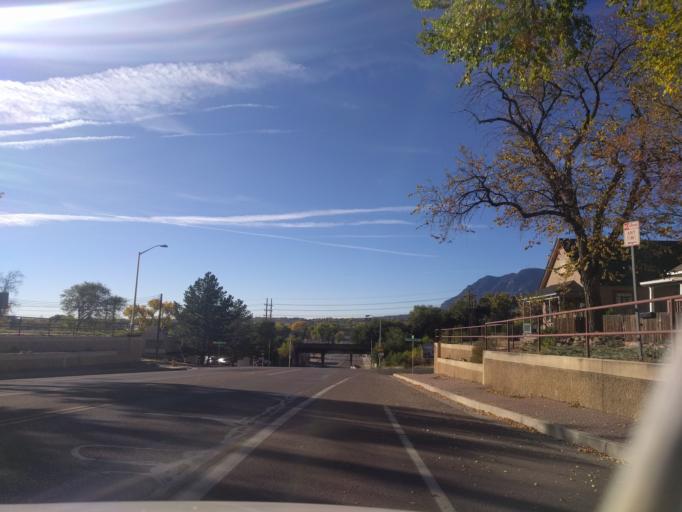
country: US
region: Colorado
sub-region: El Paso County
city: Colorado Springs
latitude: 38.8223
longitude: -104.8242
